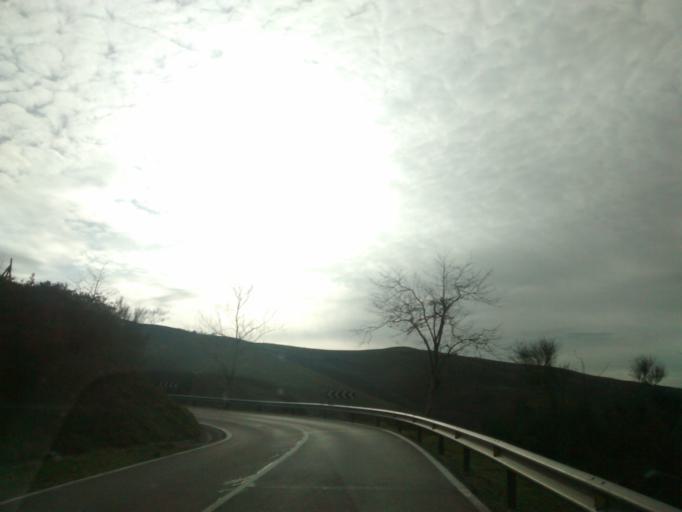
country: ES
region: Cantabria
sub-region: Provincia de Cantabria
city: Ruente
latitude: 43.2506
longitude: -4.3488
